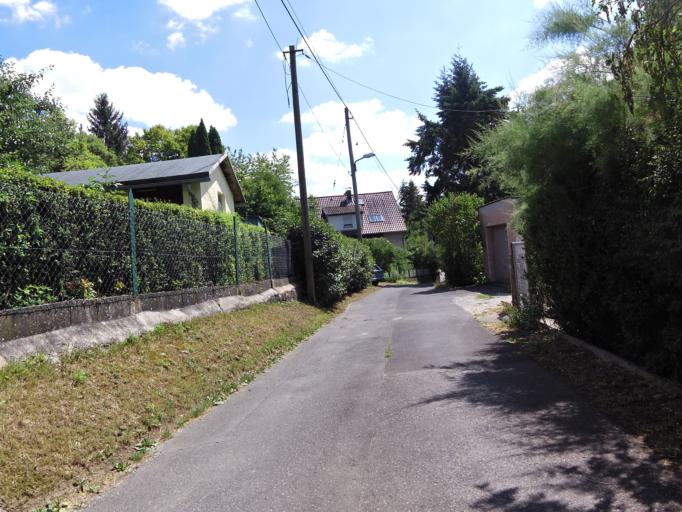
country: DE
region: Bavaria
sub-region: Regierungsbezirk Unterfranken
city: Hochberg
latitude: 49.7764
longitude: 9.8989
